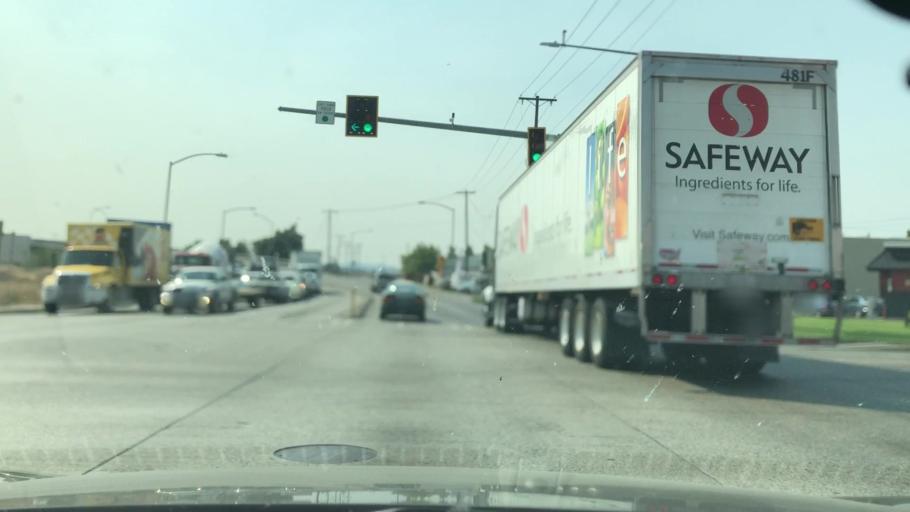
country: US
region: Washington
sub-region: Spokane County
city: Spokane
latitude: 47.6720
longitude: -117.3638
